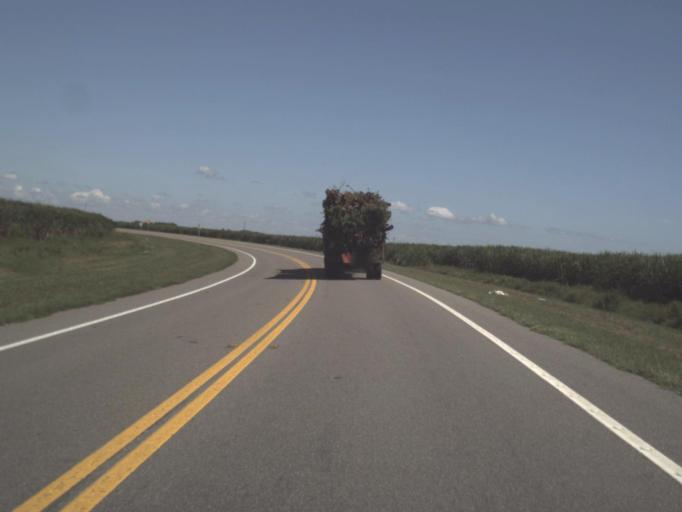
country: US
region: Florida
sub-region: Glades County
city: Moore Haven
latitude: 26.8288
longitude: -81.1878
